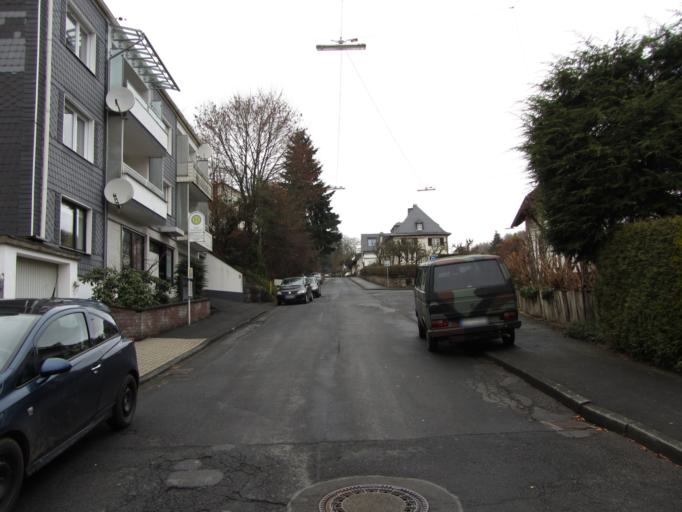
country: DE
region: North Rhine-Westphalia
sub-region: Regierungsbezirk Arnsberg
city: Siegen
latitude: 50.8836
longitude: 8.0085
